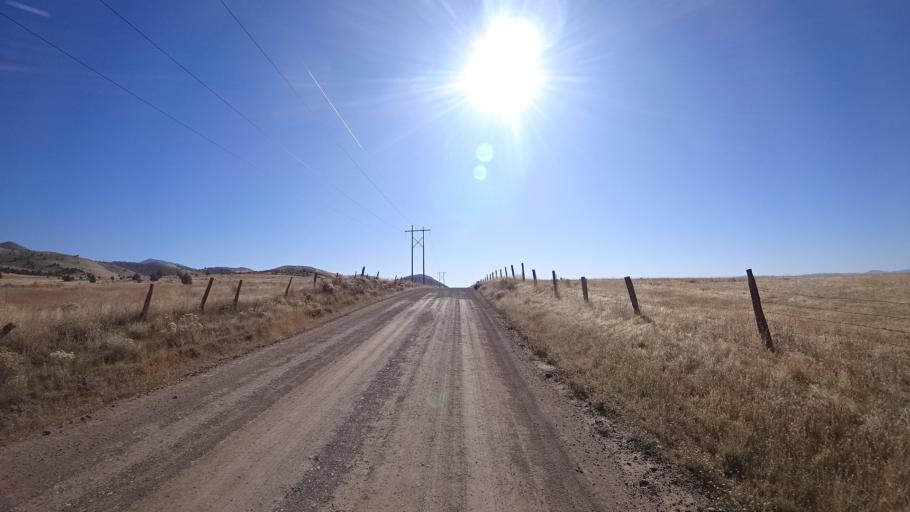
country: US
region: California
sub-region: Siskiyou County
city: Montague
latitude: 41.8268
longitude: -122.3624
